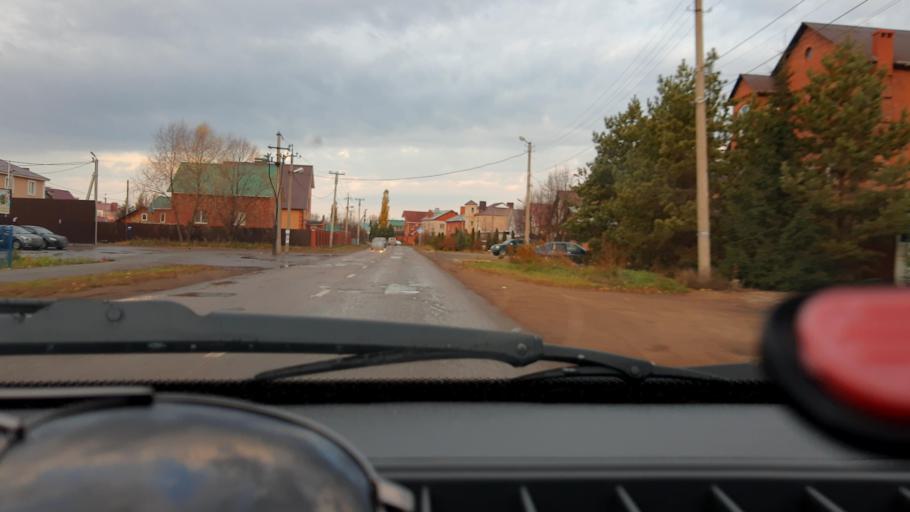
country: RU
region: Bashkortostan
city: Ufa
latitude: 54.7915
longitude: 55.9476
